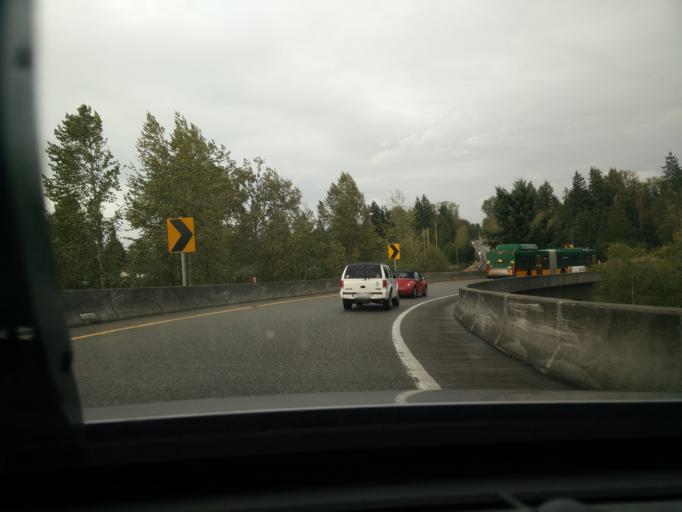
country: US
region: Washington
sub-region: Snohomish County
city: Alderwood Manor
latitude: 47.8342
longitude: -122.2644
